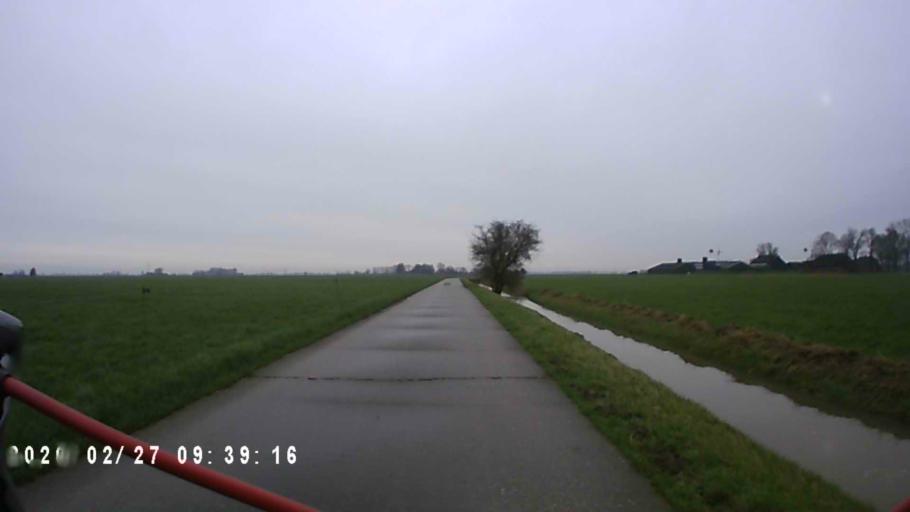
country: NL
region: Groningen
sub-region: Gemeente Zuidhorn
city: Aduard
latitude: 53.2780
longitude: 6.4322
